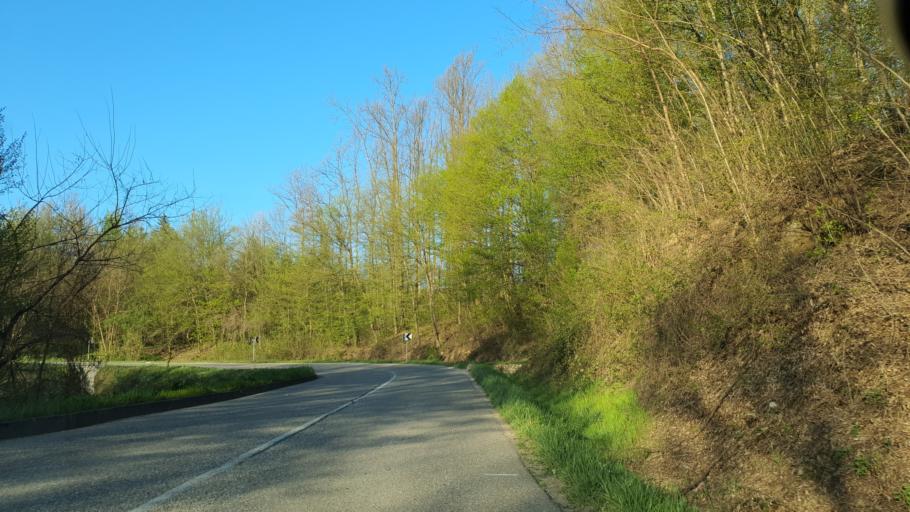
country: RS
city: Bukor
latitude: 44.4721
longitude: 19.4890
